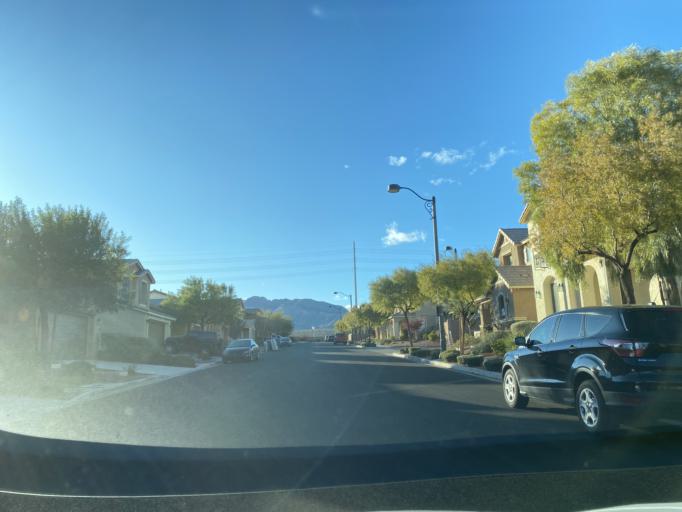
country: US
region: Nevada
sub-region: Clark County
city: Summerlin South
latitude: 36.2958
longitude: -115.3312
